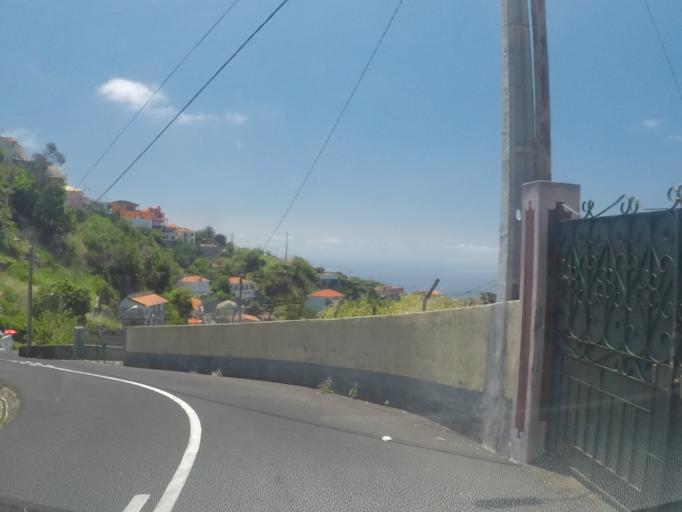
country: PT
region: Madeira
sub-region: Camara de Lobos
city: Curral das Freiras
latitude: 32.6846
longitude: -16.9927
